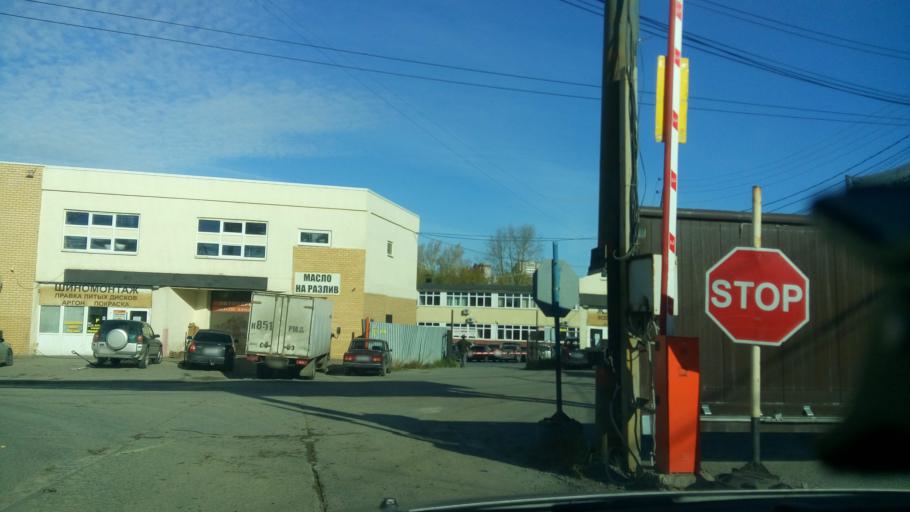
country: RU
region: Sverdlovsk
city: Sovkhoznyy
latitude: 56.7707
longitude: 60.6314
